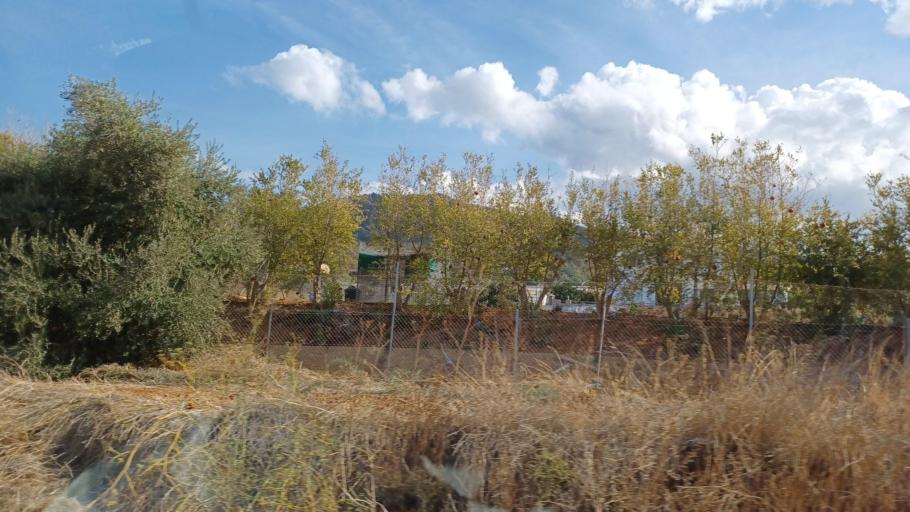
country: CY
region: Pafos
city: Polis
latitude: 35.1370
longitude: 32.5216
